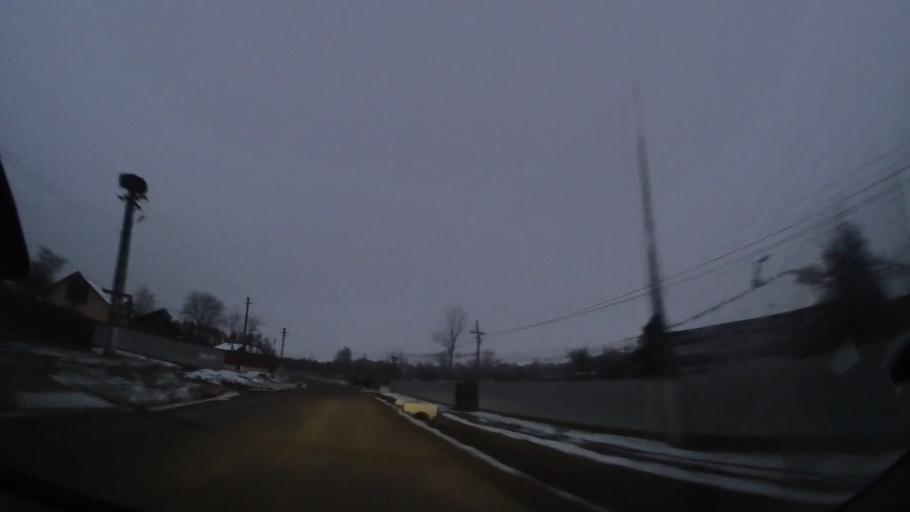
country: RO
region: Vaslui
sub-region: Comuna Dimitrie Cantemir
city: Dimitrie Cantemir
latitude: 46.5008
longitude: 28.0543
